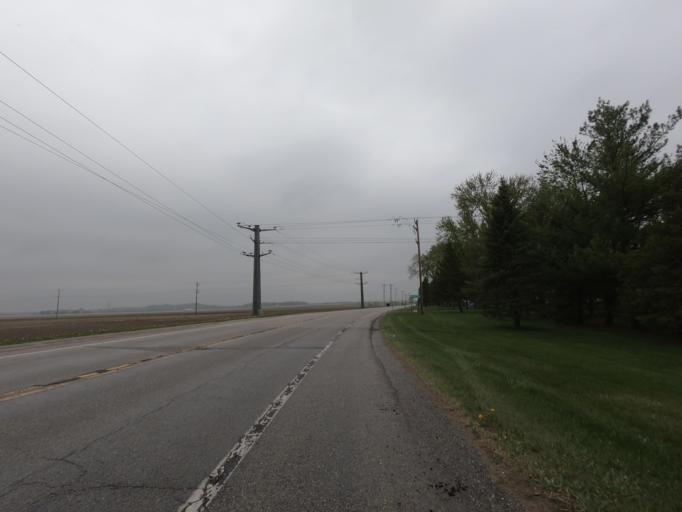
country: US
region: Wisconsin
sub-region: Jefferson County
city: Jefferson
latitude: 43.0210
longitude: -88.8186
